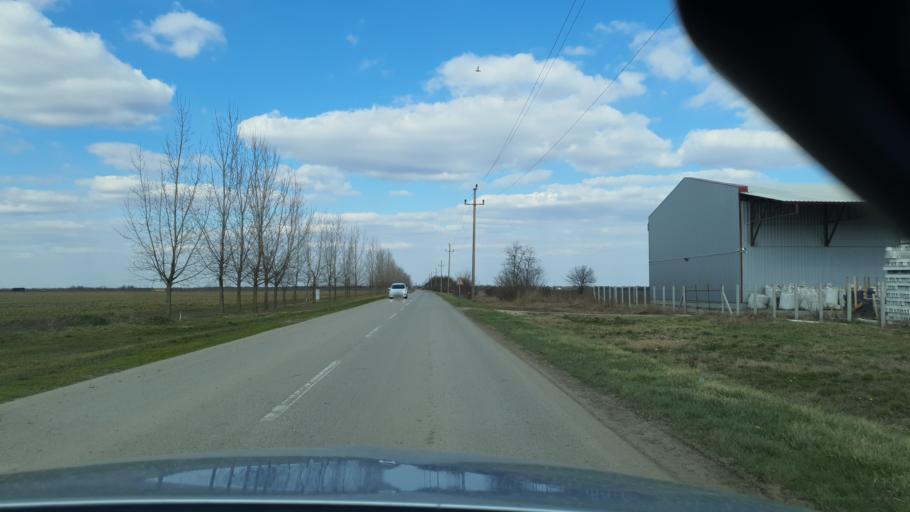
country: RS
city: Kulpin
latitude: 45.4217
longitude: 19.5996
